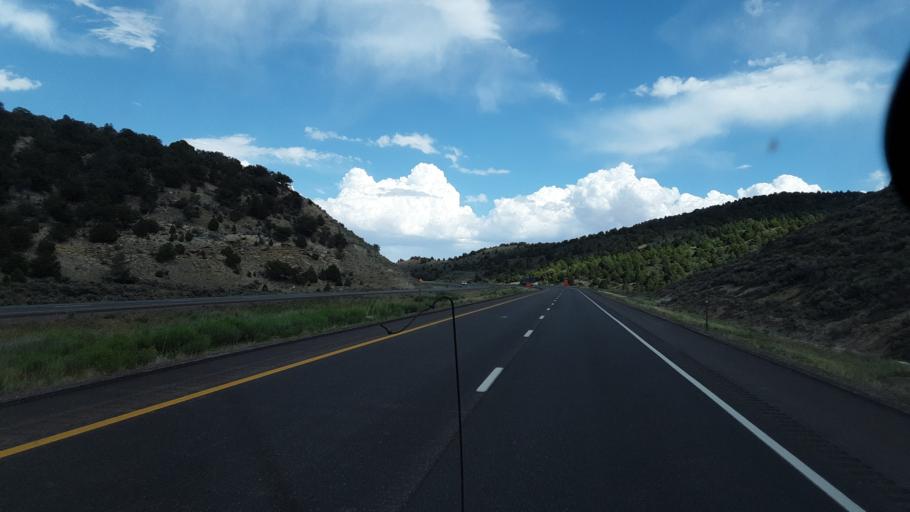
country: US
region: Utah
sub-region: Sevier County
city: Salina
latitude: 38.8083
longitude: -111.5300
